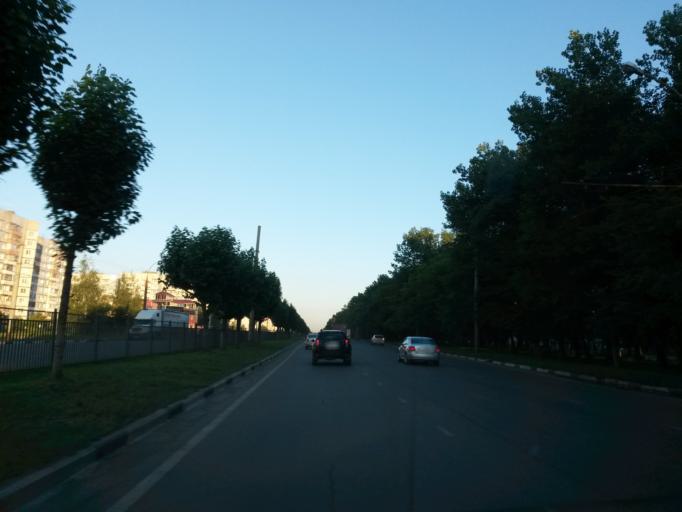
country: RU
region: Jaroslavl
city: Yaroslavl
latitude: 57.6949
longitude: 39.7688
